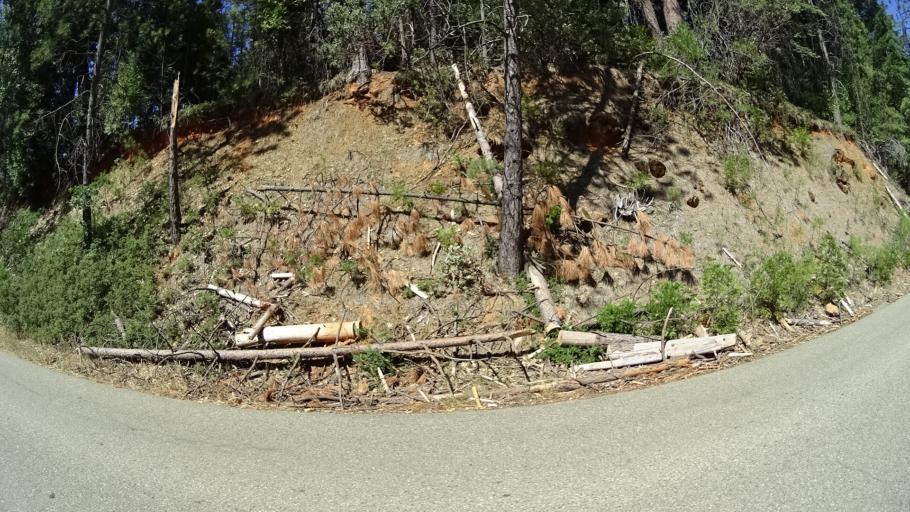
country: US
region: California
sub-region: Amador County
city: Pioneer
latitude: 38.4198
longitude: -120.4914
